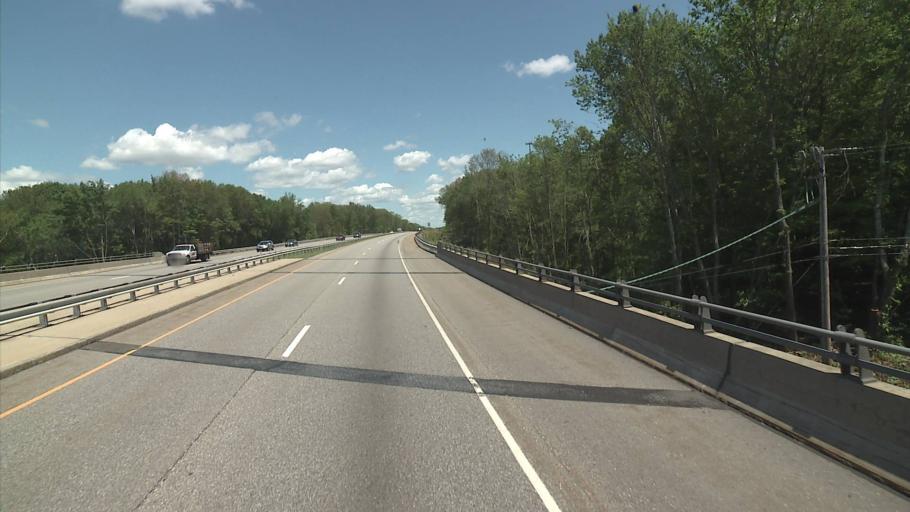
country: US
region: Connecticut
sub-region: New London County
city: Jewett City
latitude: 41.6212
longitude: -71.9442
